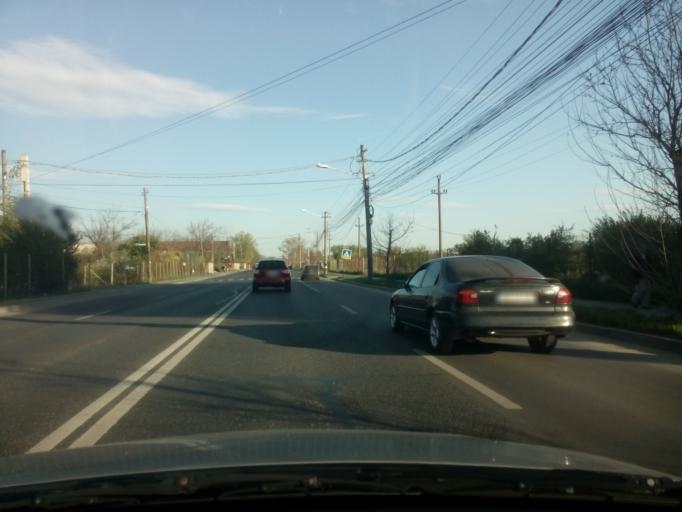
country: RO
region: Ilfov
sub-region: Comuna Mogosoaia
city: Mogosoaia
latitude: 44.5096
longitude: 26.0222
